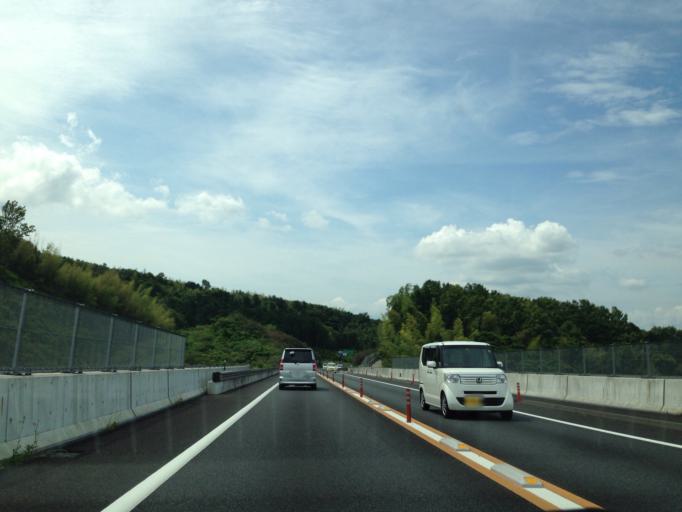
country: JP
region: Shizuoka
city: Mishima
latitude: 35.1045
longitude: 138.9481
